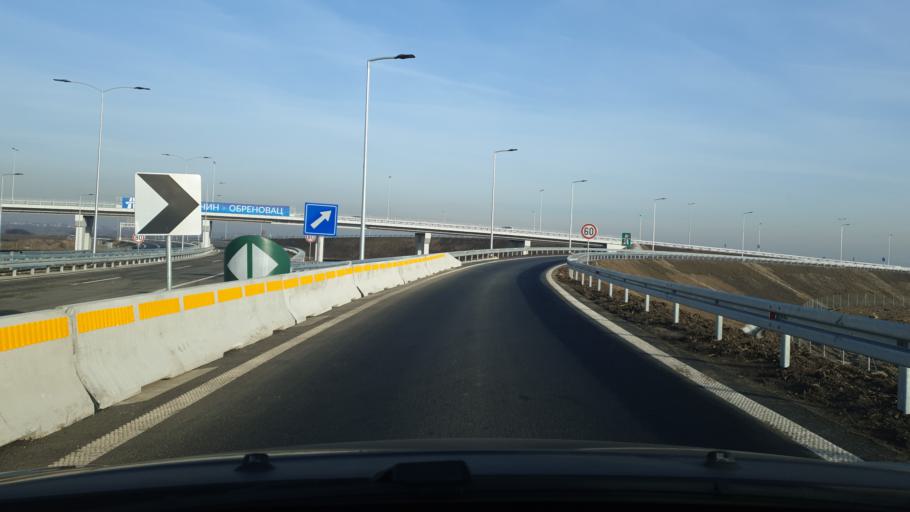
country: RS
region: Central Serbia
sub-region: Belgrade
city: Surcin
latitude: 44.7742
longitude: 20.2779
